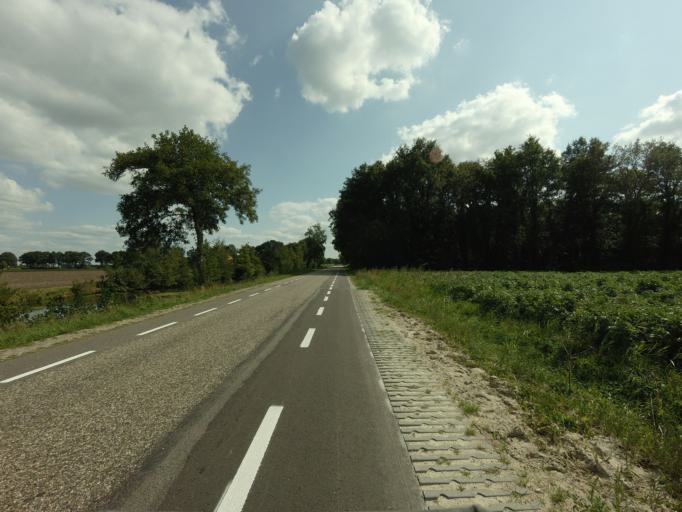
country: NL
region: Drenthe
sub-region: Gemeente Westerveld
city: Dwingeloo
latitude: 52.8650
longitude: 6.4576
